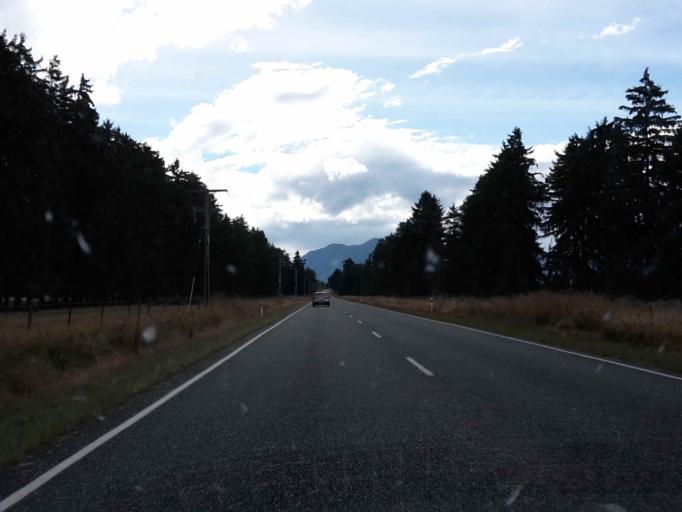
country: NZ
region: Otago
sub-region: Queenstown-Lakes District
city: Wanaka
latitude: -44.7276
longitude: 169.1369
